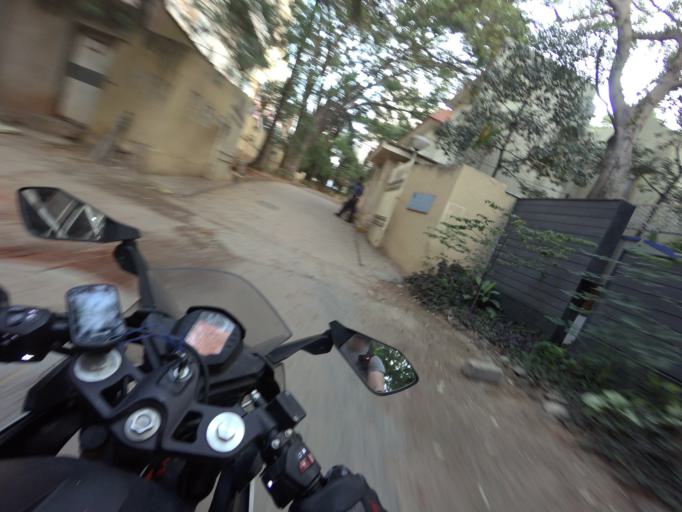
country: IN
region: Karnataka
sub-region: Bangalore Urban
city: Bangalore
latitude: 12.9740
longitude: 77.6215
